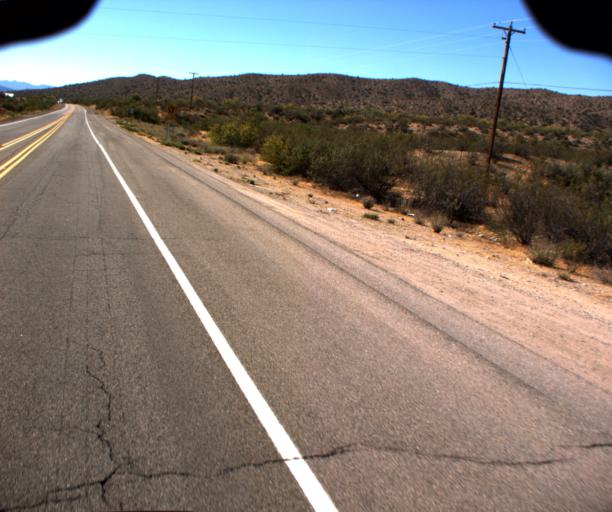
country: US
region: Arizona
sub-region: Yavapai County
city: Bagdad
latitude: 34.6976
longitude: -113.6085
